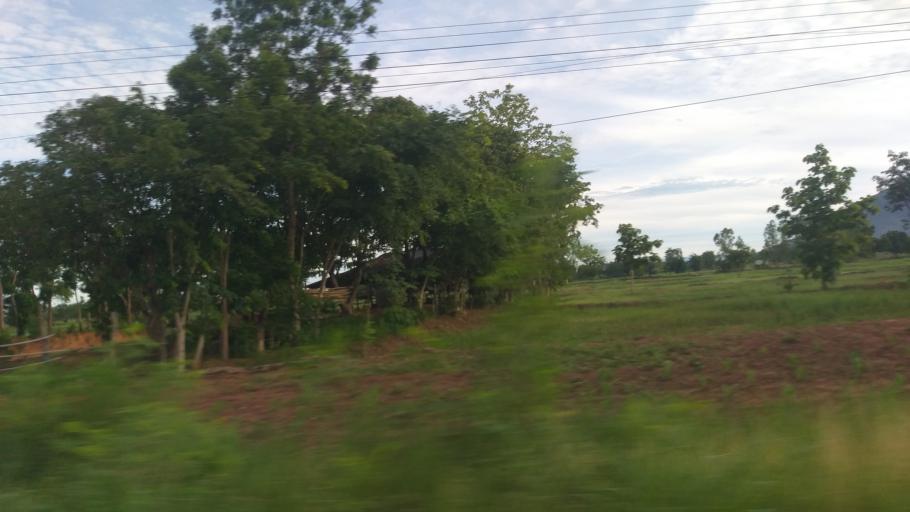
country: TH
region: Chaiyaphum
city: Phu Khiao
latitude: 16.3287
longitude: 102.2172
